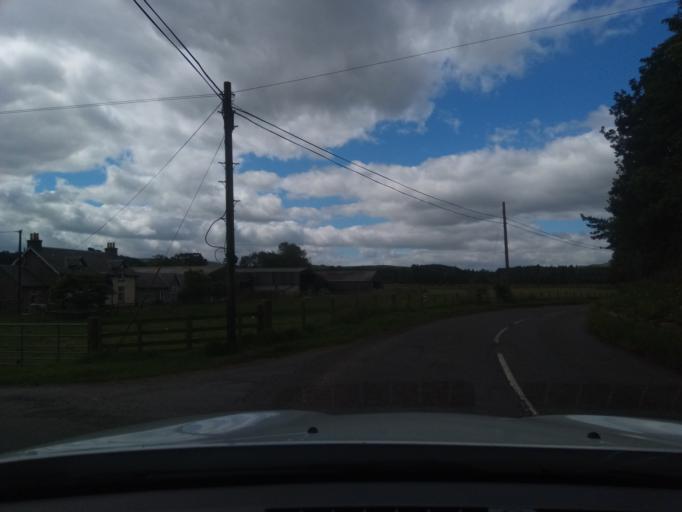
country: GB
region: Scotland
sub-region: The Scottish Borders
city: Selkirk
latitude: 55.5410
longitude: -2.8727
